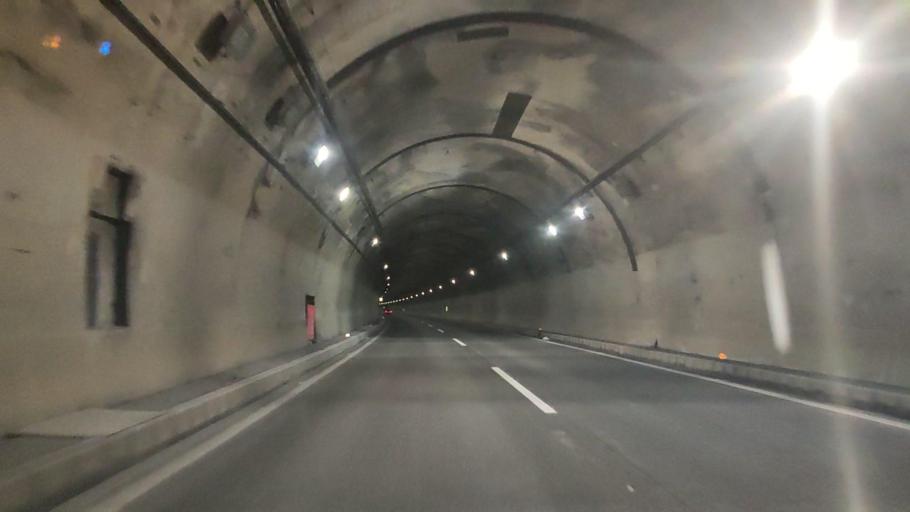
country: JP
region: Oita
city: Beppu
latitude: 33.2699
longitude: 131.3410
